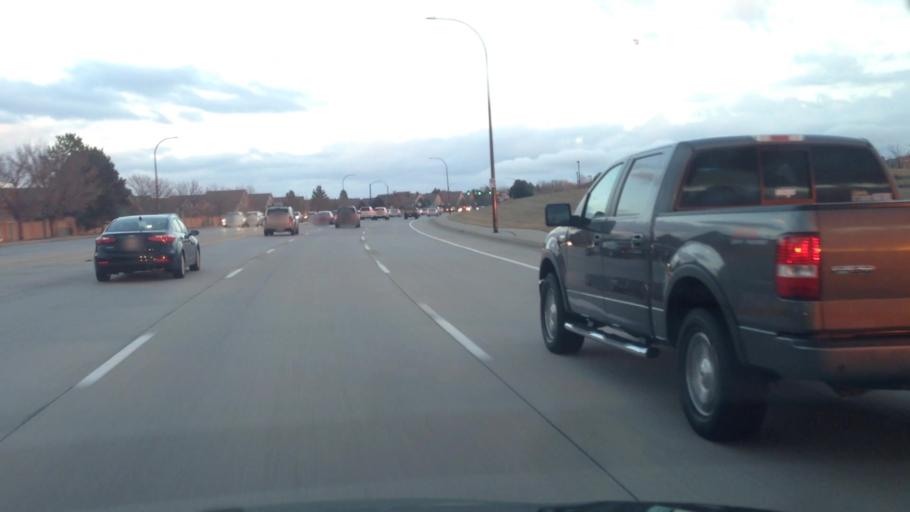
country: US
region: Colorado
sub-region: Douglas County
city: Carriage Club
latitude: 39.5442
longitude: -104.9183
